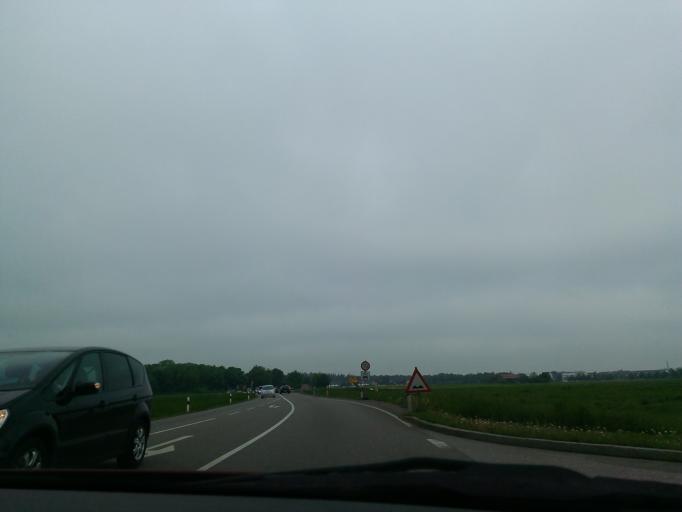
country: DE
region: Bavaria
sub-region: Upper Bavaria
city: Puchheim
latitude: 48.1527
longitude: 11.3385
